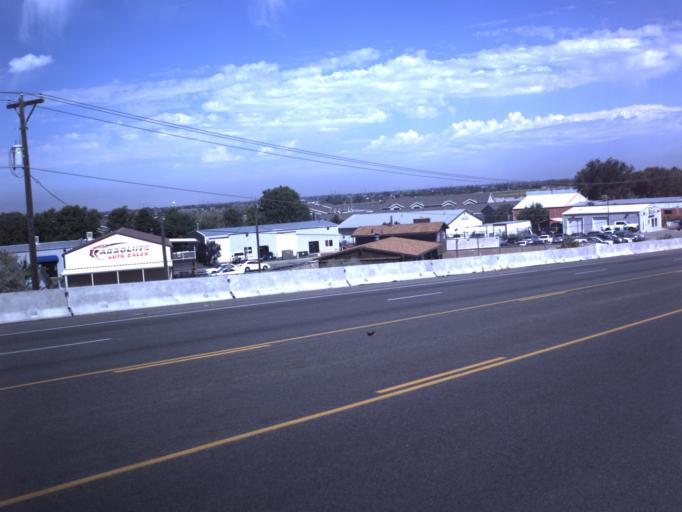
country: US
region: Utah
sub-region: Weber County
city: West Haven
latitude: 41.2023
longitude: -112.0257
